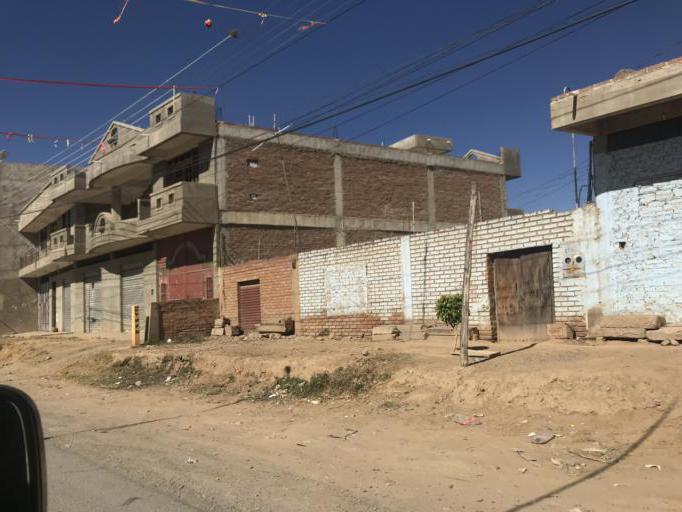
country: BO
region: Cochabamba
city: Cliza
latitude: -17.5892
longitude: -65.9262
